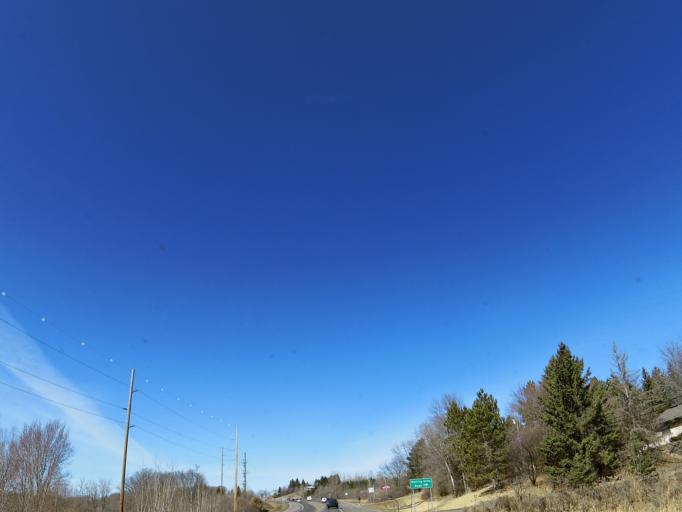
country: US
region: Minnesota
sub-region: Hennepin County
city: Medina
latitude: 45.0633
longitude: -93.6017
